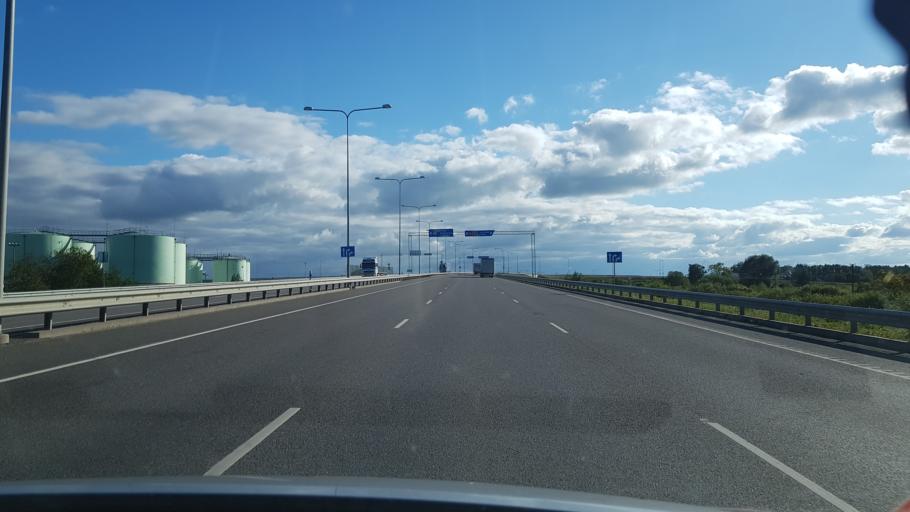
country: EE
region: Harju
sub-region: Joelaehtme vald
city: Loo
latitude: 59.4540
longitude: 24.9839
